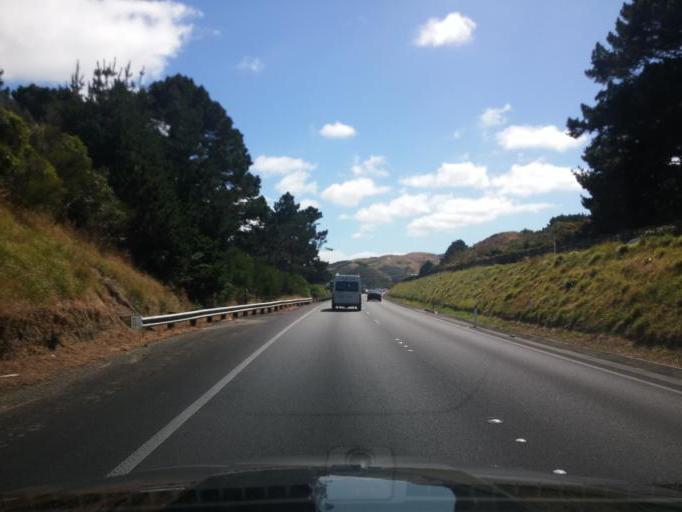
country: NZ
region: Wellington
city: Petone
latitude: -41.1912
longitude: 174.8306
